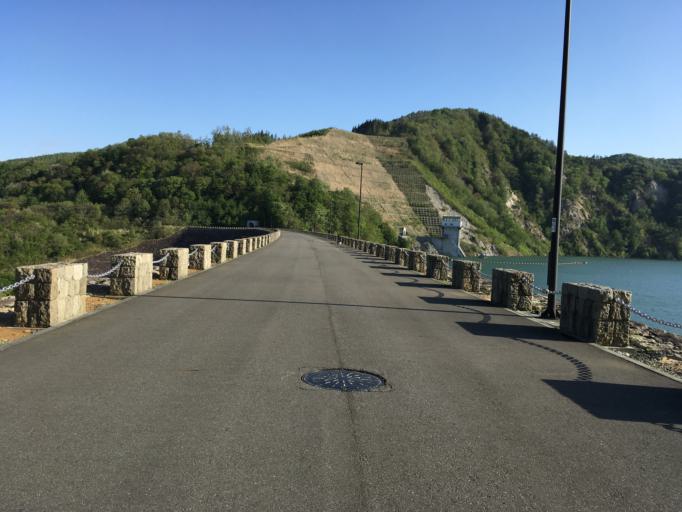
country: JP
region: Iwate
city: Mizusawa
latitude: 39.1221
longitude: 140.9198
